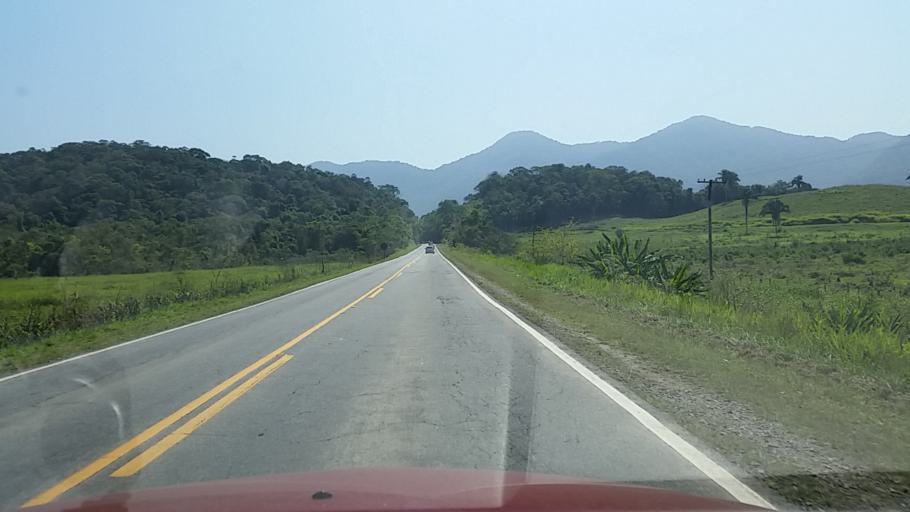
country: BR
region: Sao Paulo
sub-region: Juquia
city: Juquia
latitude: -24.3984
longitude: -47.5272
